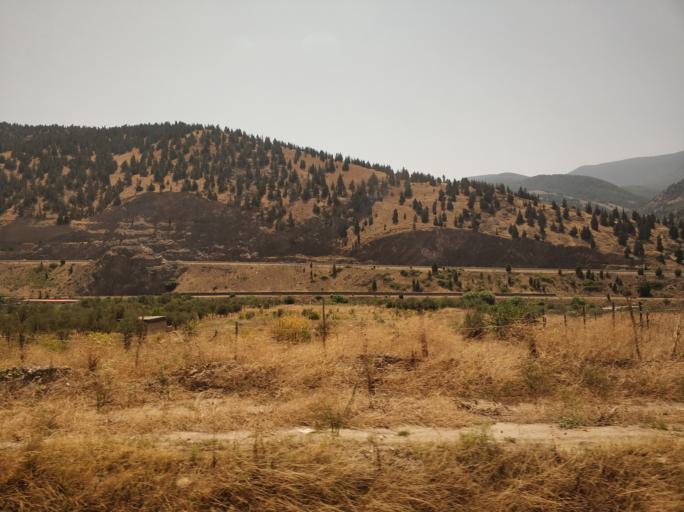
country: IR
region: Gilan
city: Pa'in-e Bazar-e Rudbar
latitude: 36.8506
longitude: 49.4761
